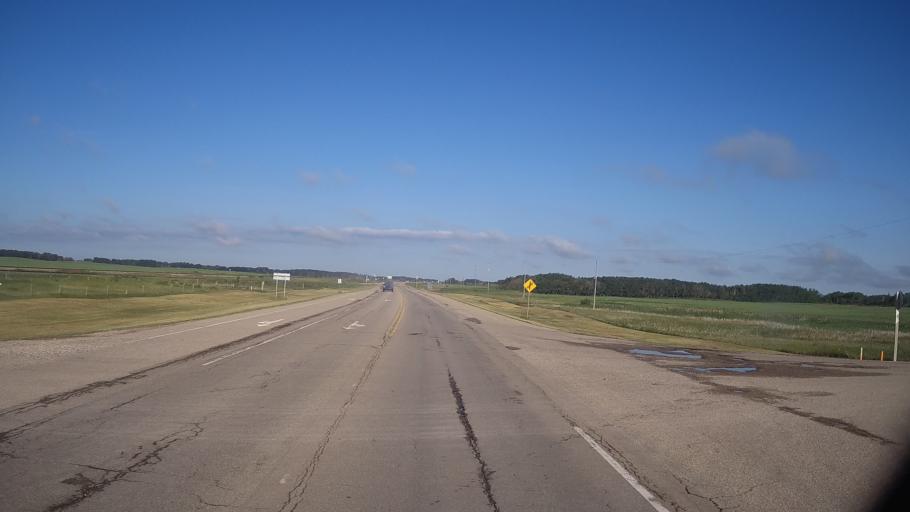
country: CA
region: Saskatchewan
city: Lanigan
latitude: 51.8491
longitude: -105.0522
